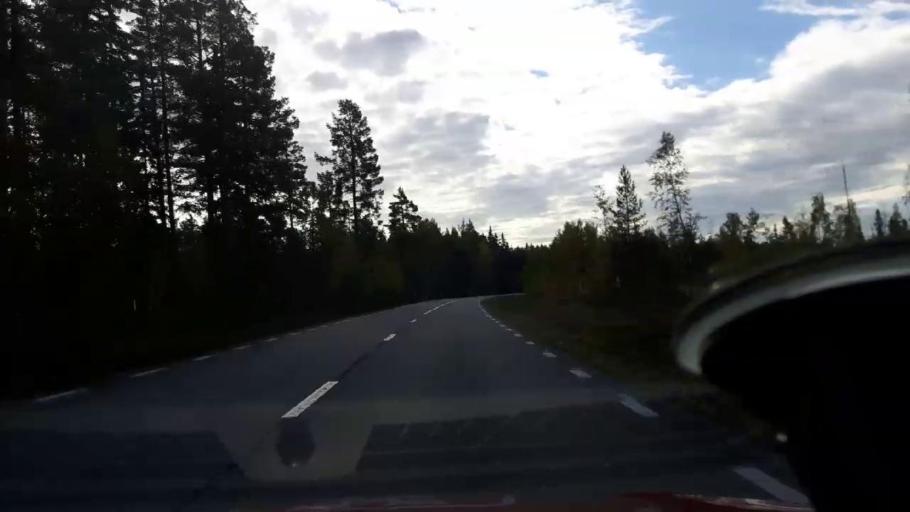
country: SE
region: Gaevleborg
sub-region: Ljusdals Kommun
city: Farila
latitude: 62.0165
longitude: 15.2384
